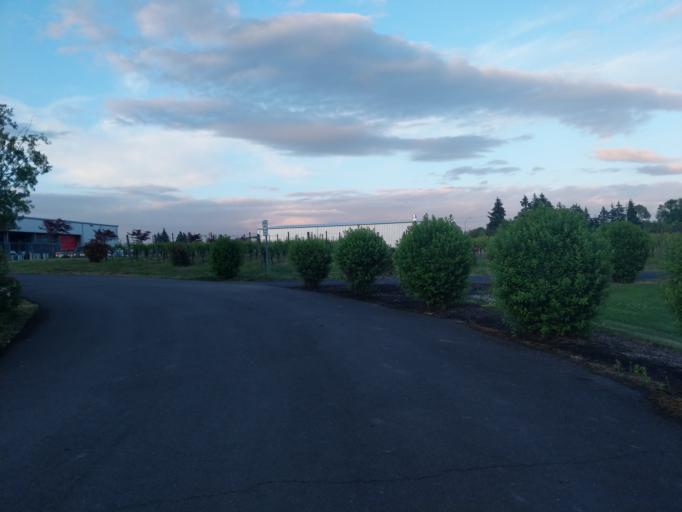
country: US
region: Oregon
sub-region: Yamhill County
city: Dundee
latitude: 45.2687
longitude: -123.0227
